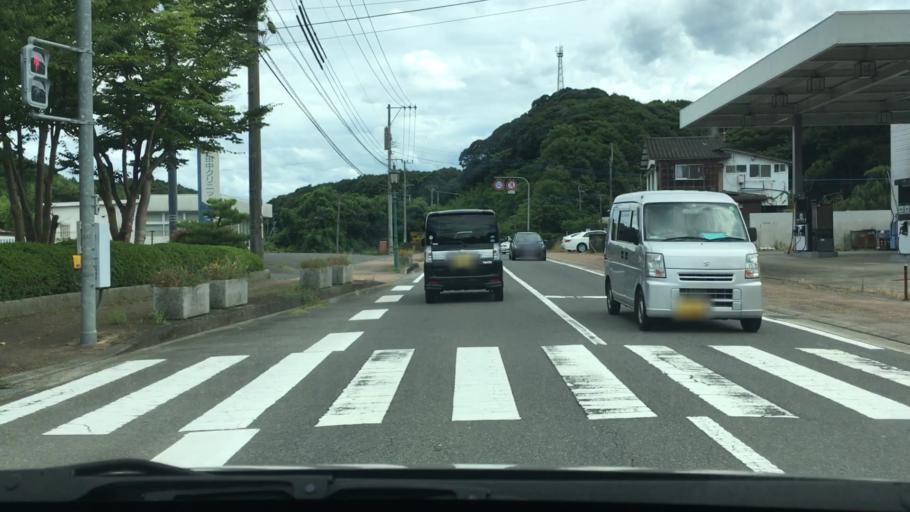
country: JP
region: Nagasaki
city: Sasebo
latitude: 32.9887
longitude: 129.7663
